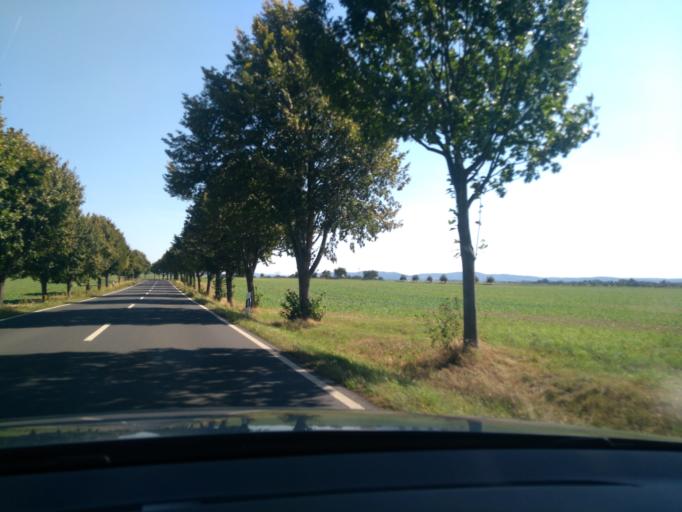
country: DE
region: Saxony
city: Crostwitz
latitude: 51.2153
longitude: 14.2683
